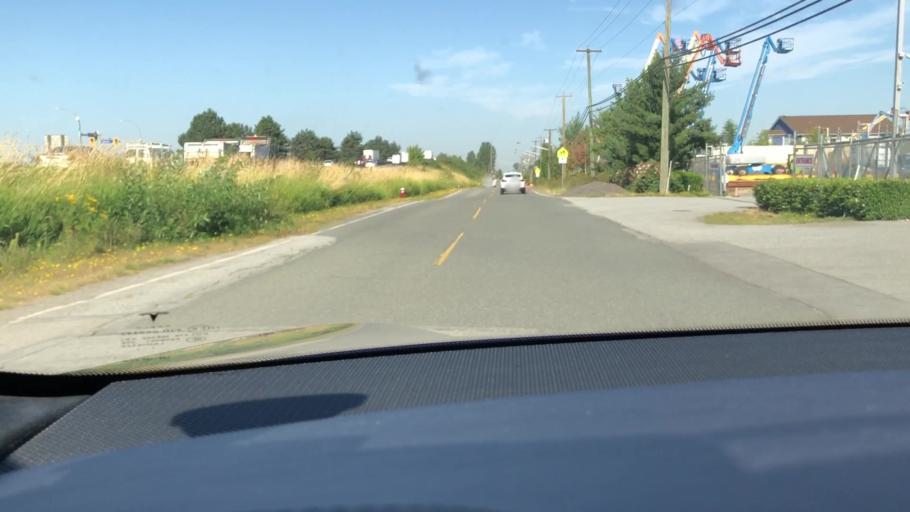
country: CA
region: British Columbia
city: Delta
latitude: 49.1699
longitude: -122.9925
